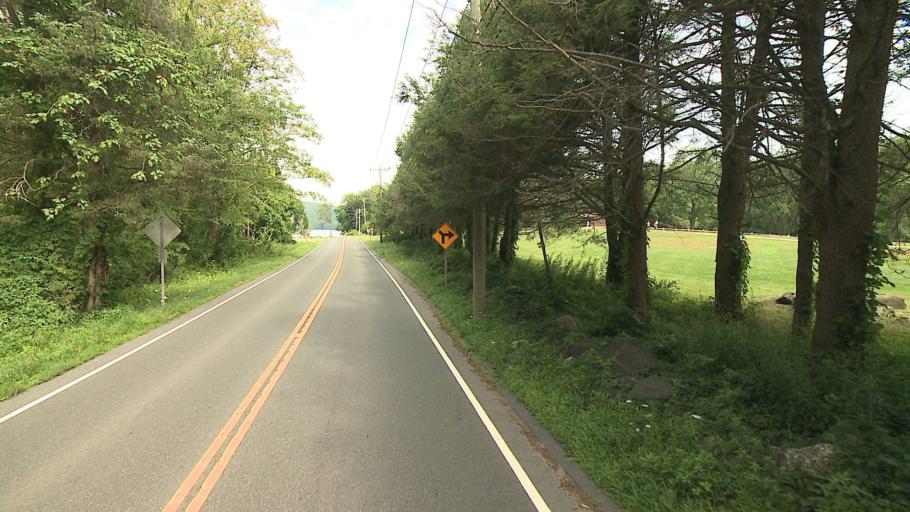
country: US
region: Connecticut
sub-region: Fairfield County
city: Sherman
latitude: 41.5080
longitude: -73.4706
